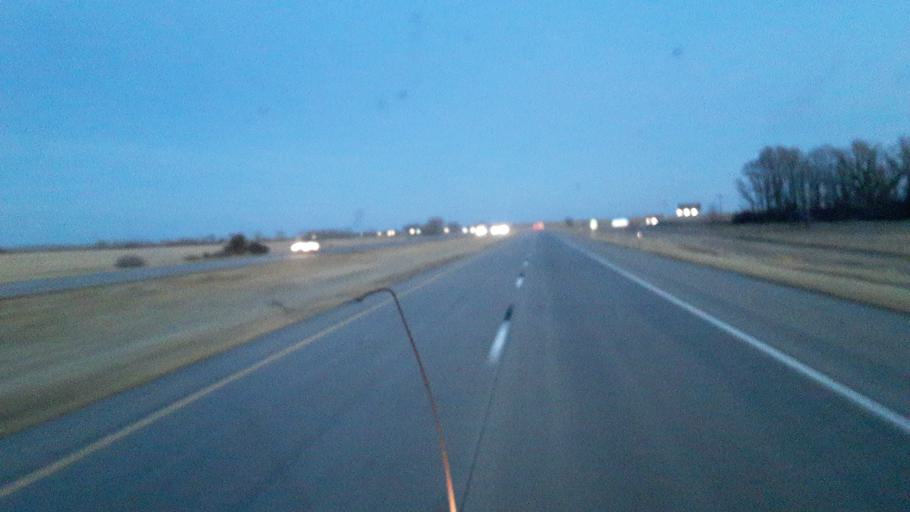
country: US
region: Nebraska
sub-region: Keith County
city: Ogallala
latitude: 41.1066
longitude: -101.4937
